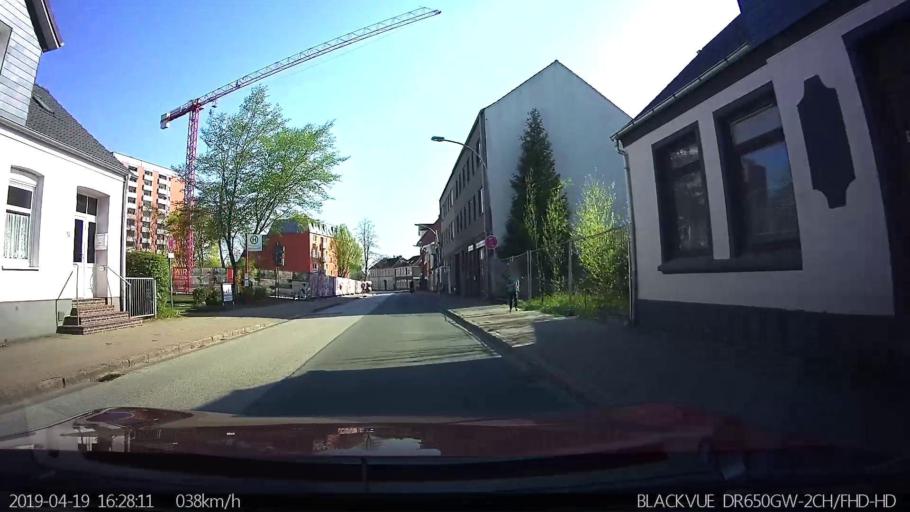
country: DE
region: Schleswig-Holstein
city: Pinneberg
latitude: 53.6600
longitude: 9.7933
